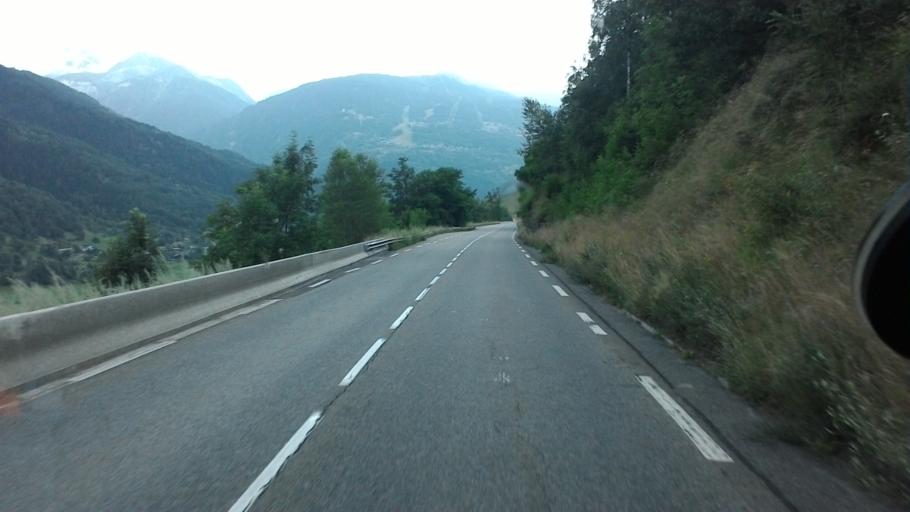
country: FR
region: Rhone-Alpes
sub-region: Departement de la Savoie
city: Bourg-Saint-Maurice
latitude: 45.5966
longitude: 6.7506
